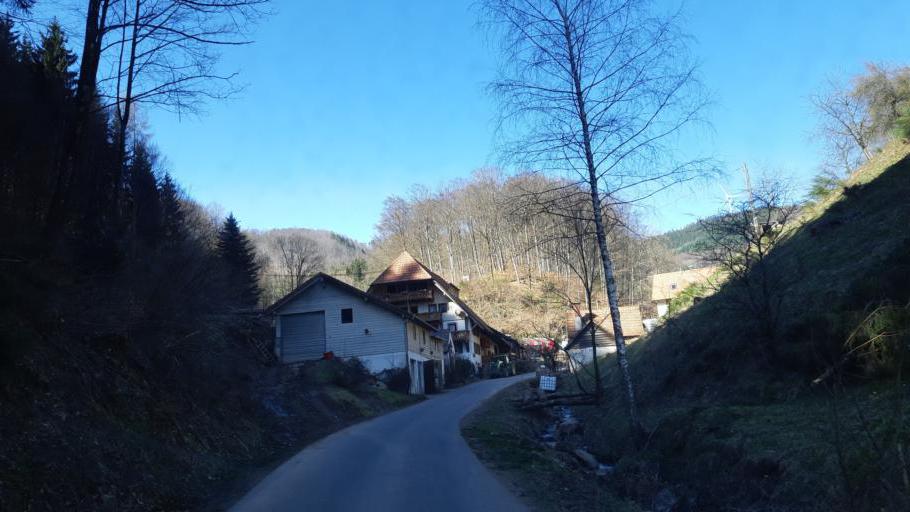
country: DE
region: Baden-Wuerttemberg
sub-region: Freiburg Region
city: Gutach im Breisgau
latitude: 48.1603
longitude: 7.9752
